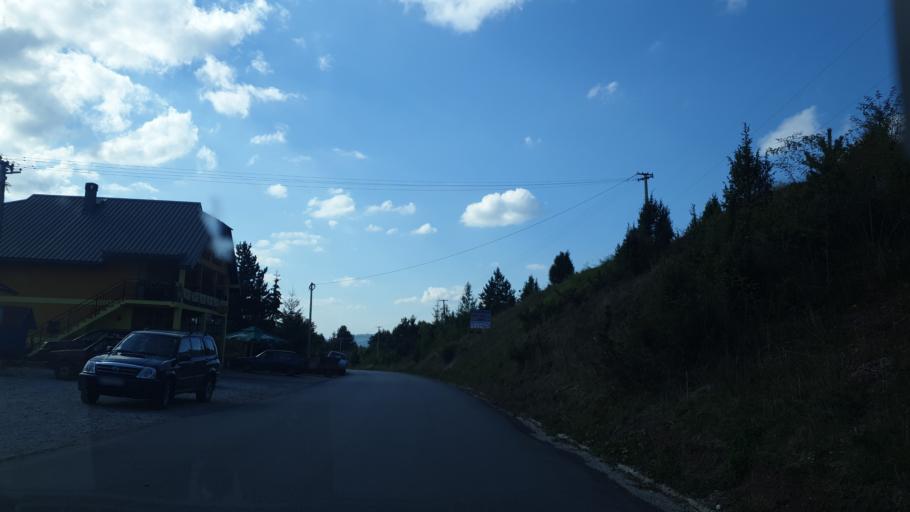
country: RS
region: Central Serbia
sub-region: Zlatiborski Okrug
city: Nova Varos
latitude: 43.4294
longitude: 19.8940
